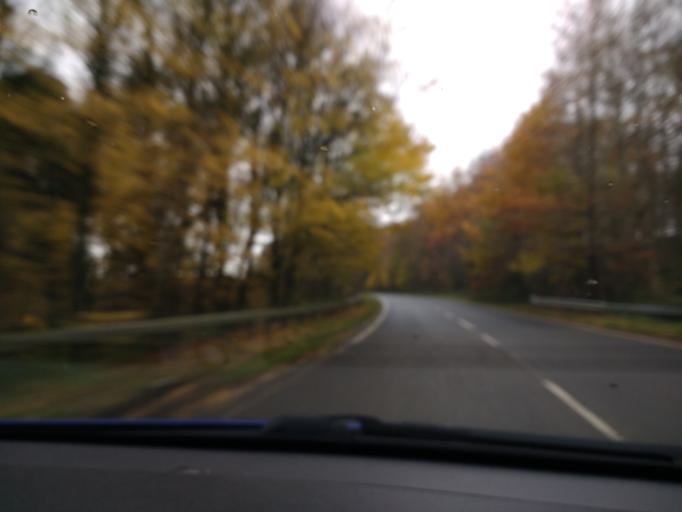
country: GB
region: England
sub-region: Cumbria
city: Millom
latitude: 54.2682
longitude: -3.2575
